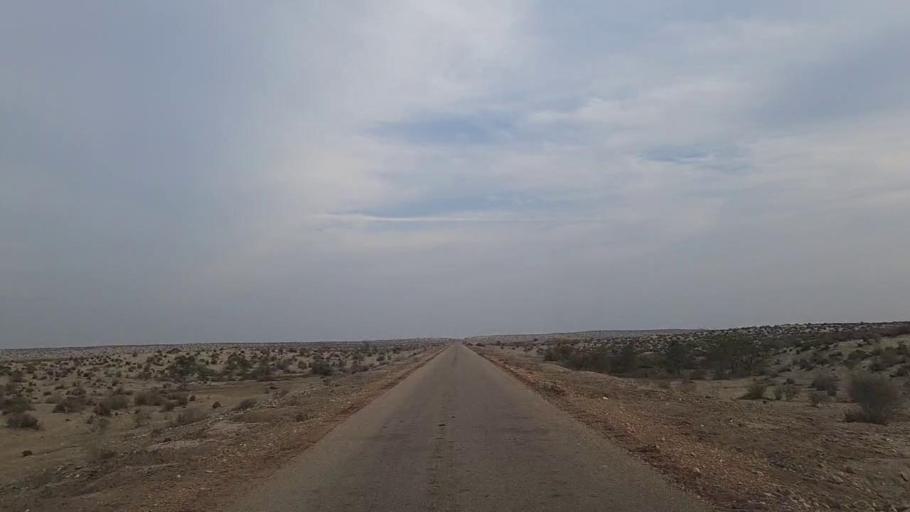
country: PK
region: Sindh
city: Daur
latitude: 26.5138
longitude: 68.5028
